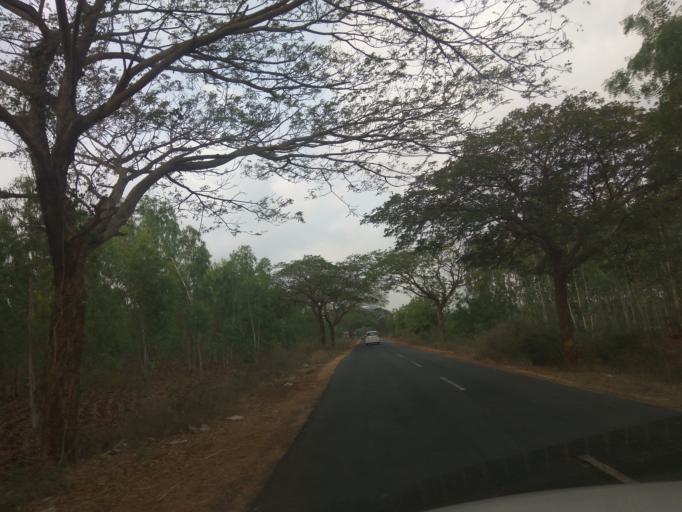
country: IN
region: Andhra Pradesh
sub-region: Prakasam
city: Kandukur
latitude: 15.1973
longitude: 79.8431
